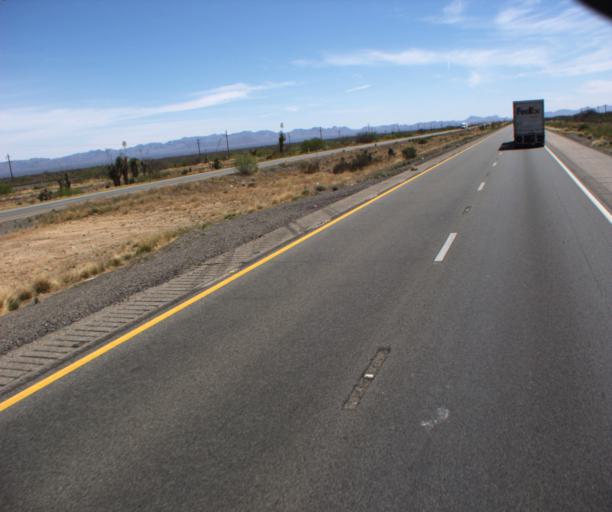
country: US
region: Arizona
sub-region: Cochise County
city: Willcox
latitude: 32.3089
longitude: -109.4053
